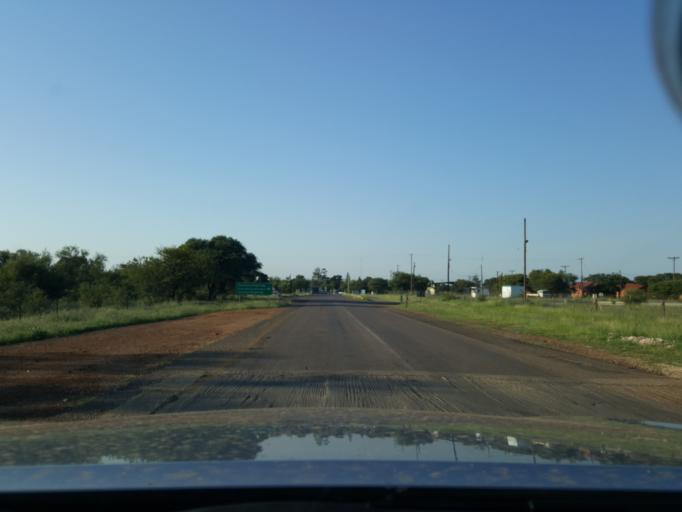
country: BW
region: South East
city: Janeng
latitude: -25.6346
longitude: 25.5742
